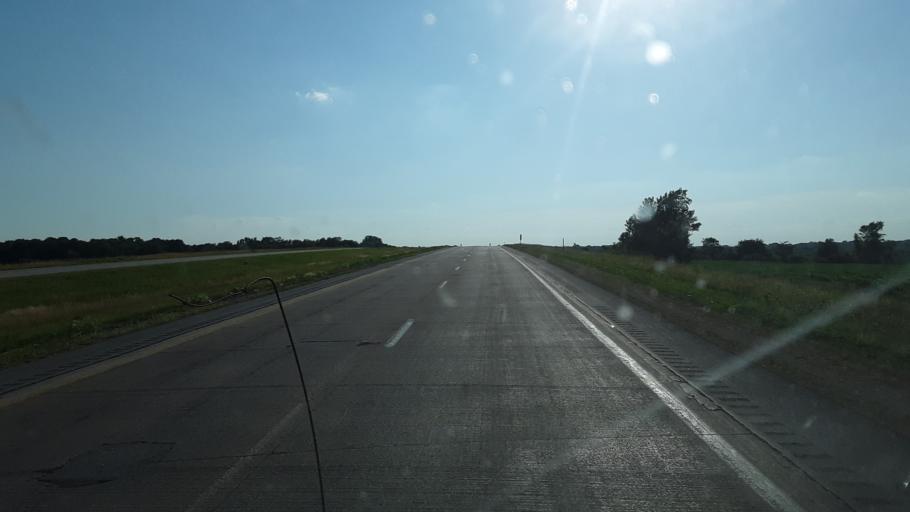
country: US
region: Iowa
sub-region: Hardin County
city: Iowa Falls
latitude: 42.4486
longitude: -93.3523
